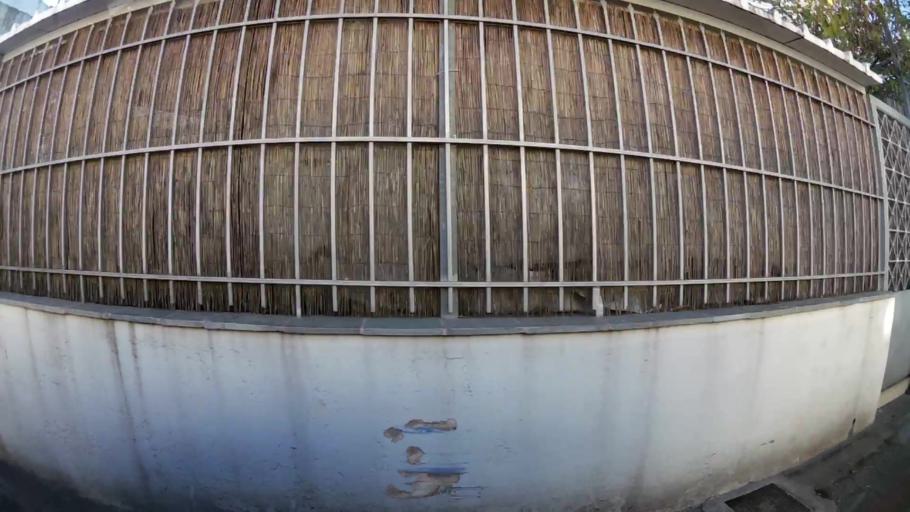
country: GR
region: Attica
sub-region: Nomarchia Anatolikis Attikis
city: Acharnes
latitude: 38.0881
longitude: 23.7225
